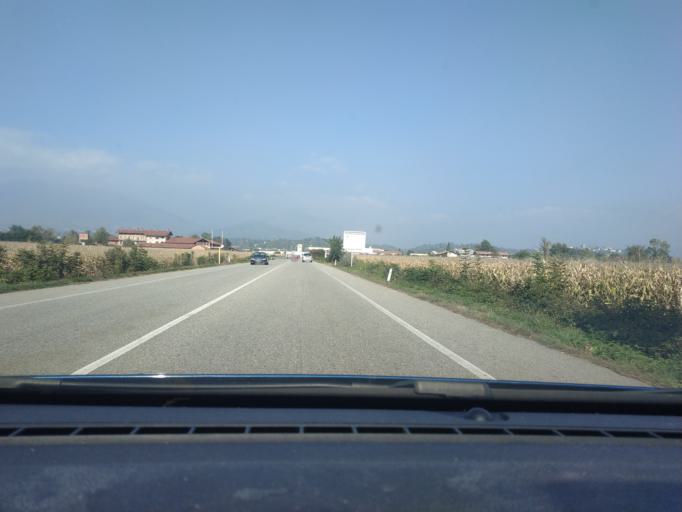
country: IT
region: Piedmont
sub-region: Provincia di Biella
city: Occhieppo Inferiore
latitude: 45.5436
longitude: 8.0372
